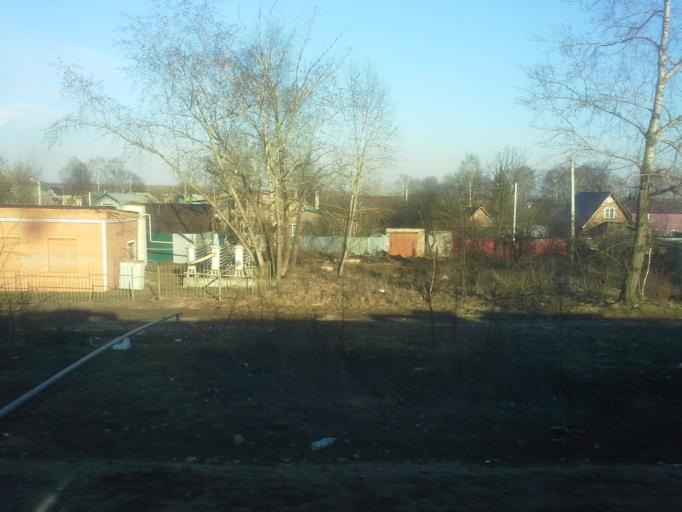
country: RU
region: Moskovskaya
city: Nekrasovskiy
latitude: 56.0919
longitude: 37.5049
